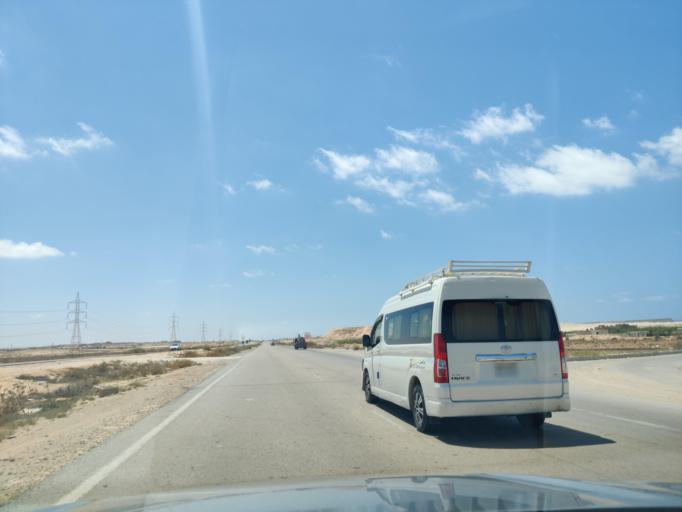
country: EG
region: Muhafazat Matruh
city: Al `Alamayn
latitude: 31.0641
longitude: 28.1954
